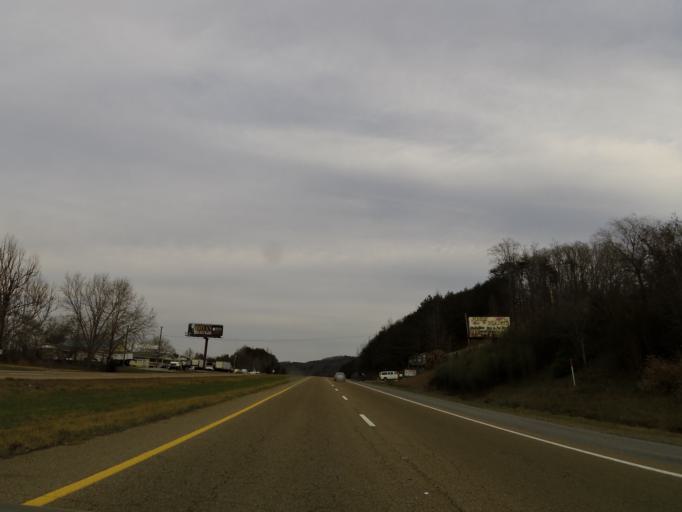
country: US
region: Tennessee
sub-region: Rhea County
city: Graysville
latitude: 35.4469
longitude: -85.0651
